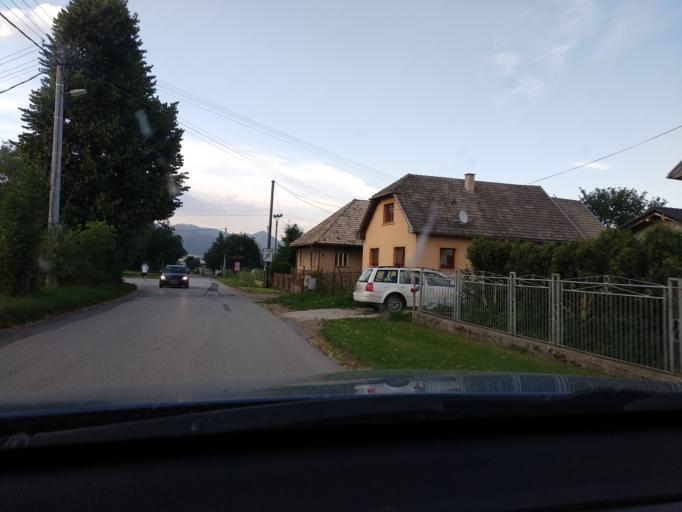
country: SK
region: Zilinsky
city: Ruzomberok
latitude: 49.0540
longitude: 19.3342
